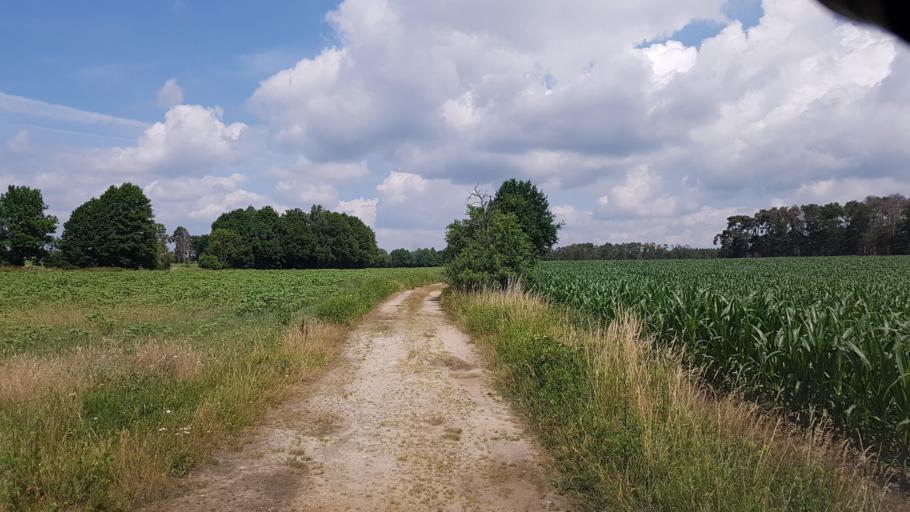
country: DE
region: Brandenburg
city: Crinitz
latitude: 51.7488
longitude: 13.8362
